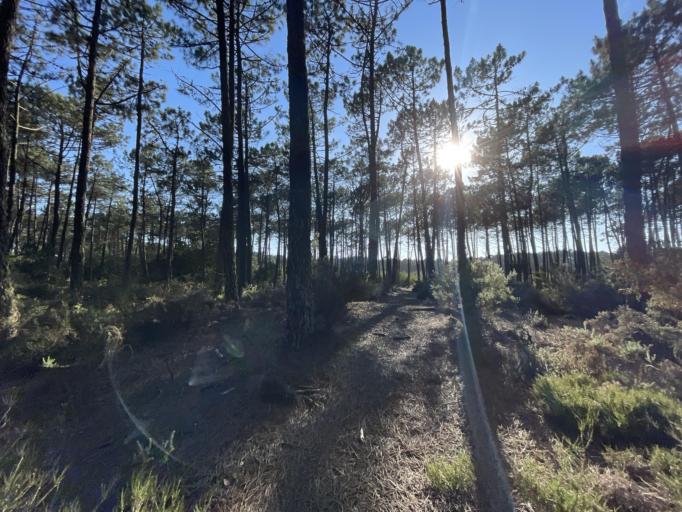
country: PT
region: Aveiro
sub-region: Ovar
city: Cortegaca
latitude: 40.9369
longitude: -8.6458
